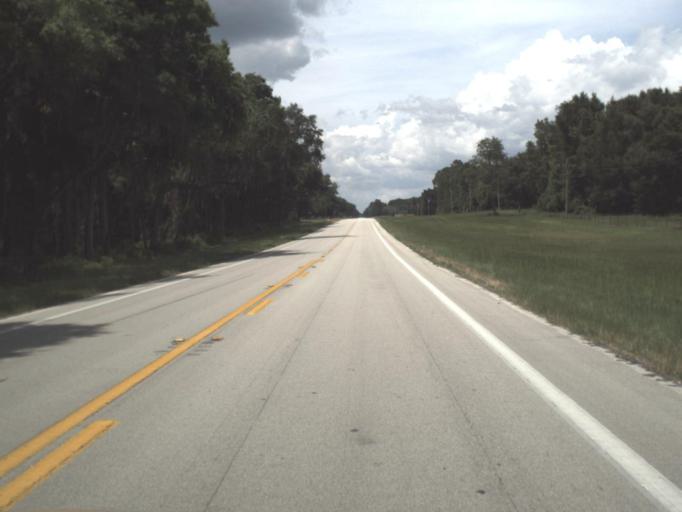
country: US
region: Florida
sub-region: Alachua County
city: High Springs
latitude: 29.7723
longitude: -82.6077
